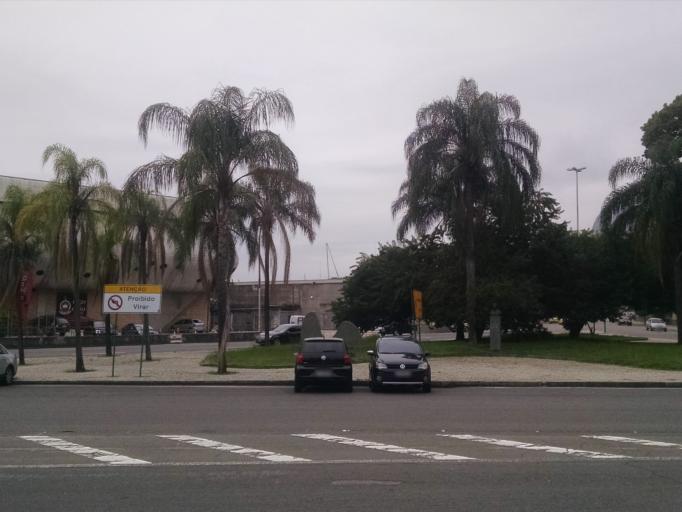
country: BR
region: Rio de Janeiro
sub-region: Rio De Janeiro
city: Rio de Janeiro
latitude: -22.9434
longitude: -43.1805
